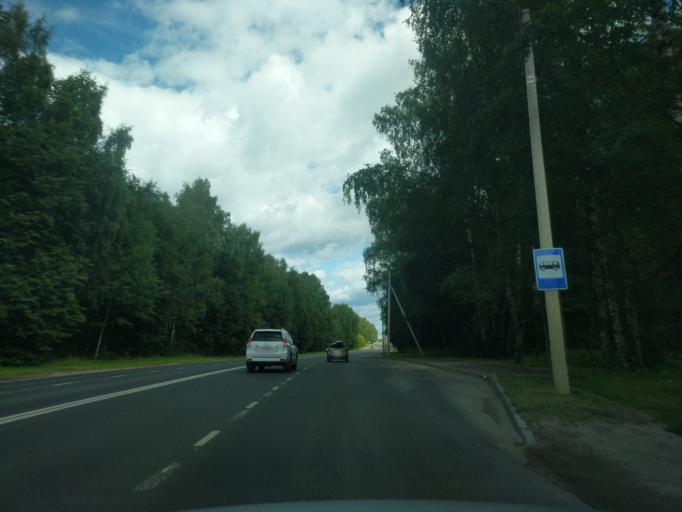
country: RU
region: Kostroma
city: Oktyabr'skiy
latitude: 57.7833
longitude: 41.0096
